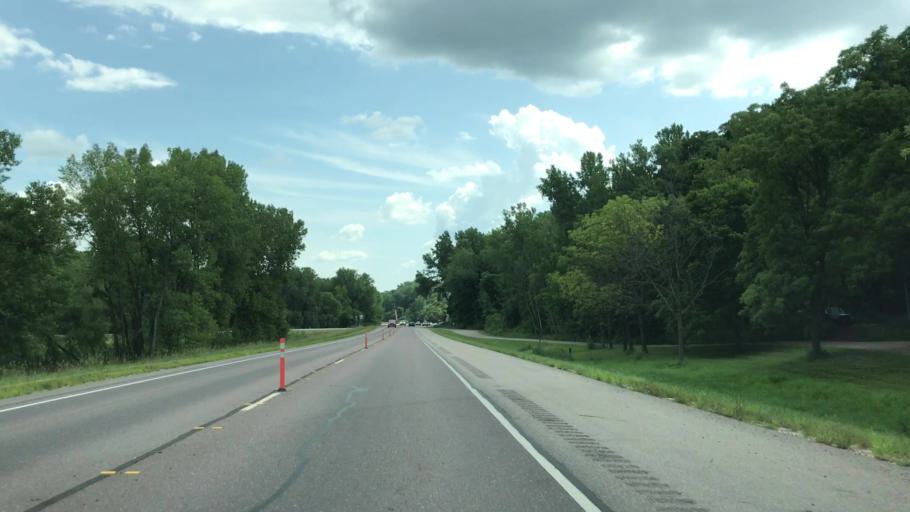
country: US
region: Minnesota
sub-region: Nicollet County
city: Saint Peter
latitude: 44.3718
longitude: -93.9666
